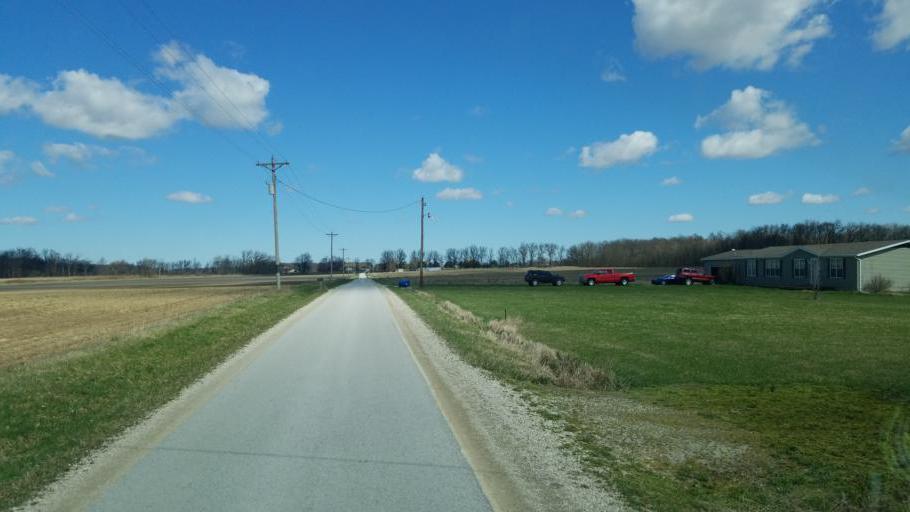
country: US
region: Ohio
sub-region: Sandusky County
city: Mount Carmel
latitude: 41.2134
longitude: -82.9373
